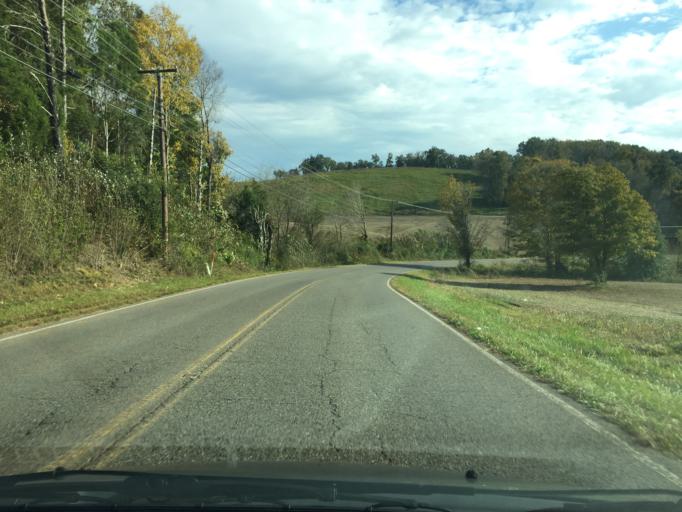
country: US
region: Tennessee
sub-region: Loudon County
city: Loudon
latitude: 35.7144
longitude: -84.3454
